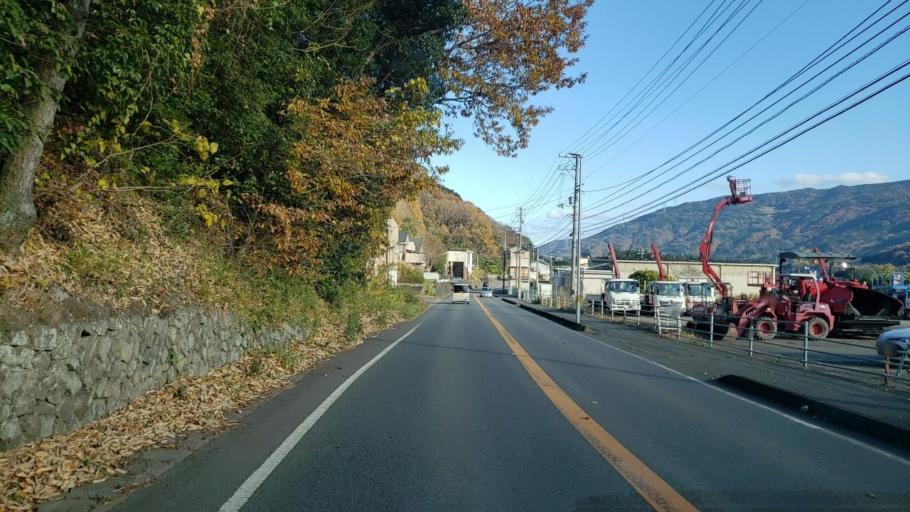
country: JP
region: Tokushima
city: Wakimachi
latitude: 34.0608
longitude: 134.0815
